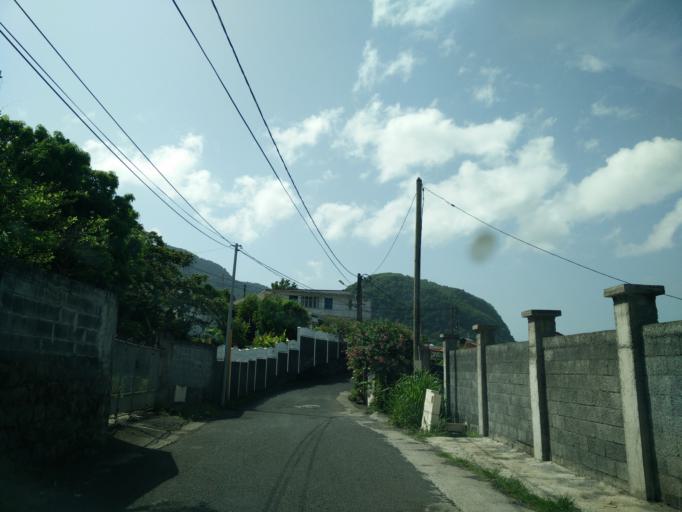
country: GP
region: Guadeloupe
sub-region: Guadeloupe
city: Gourbeyre
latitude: 15.9944
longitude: -61.7075
